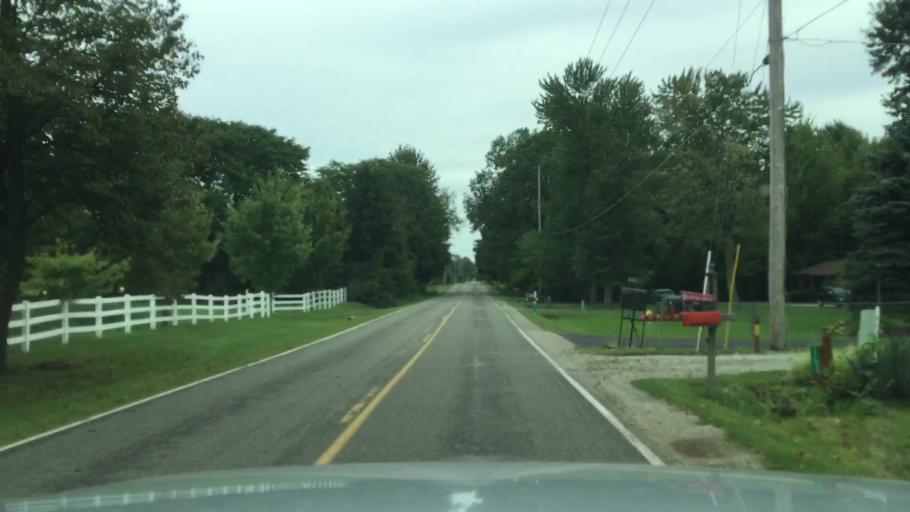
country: US
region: Michigan
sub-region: Shiawassee County
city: Durand
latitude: 42.9516
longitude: -83.9378
